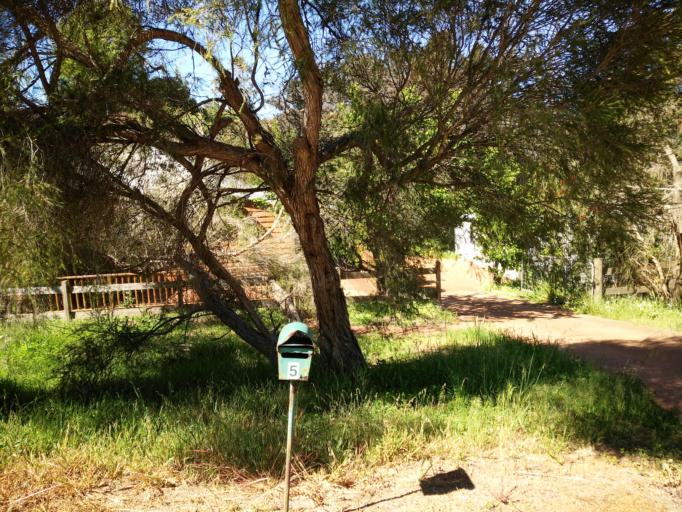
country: AU
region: Western Australia
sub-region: Bridgetown-Greenbushes
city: Bridgetown
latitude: -33.9572
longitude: 116.1433
